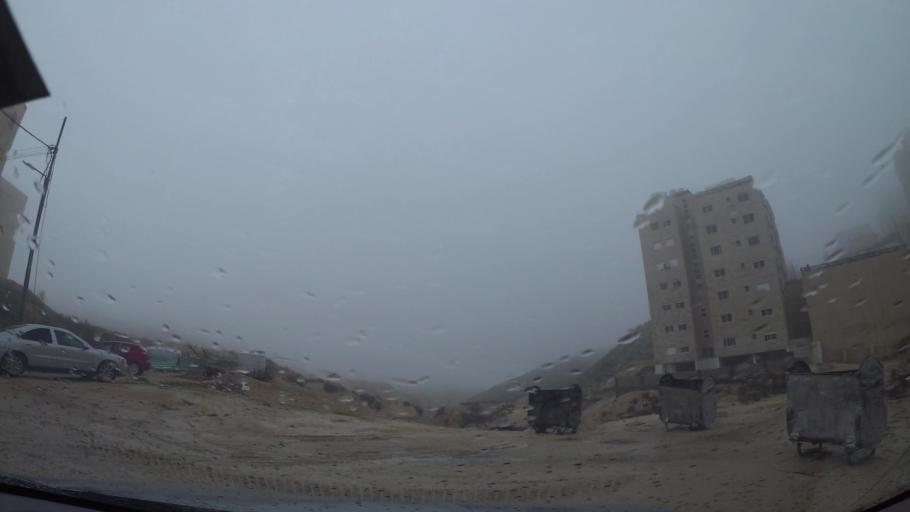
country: JO
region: Amman
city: Al Jubayhah
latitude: 32.0095
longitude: 35.8879
